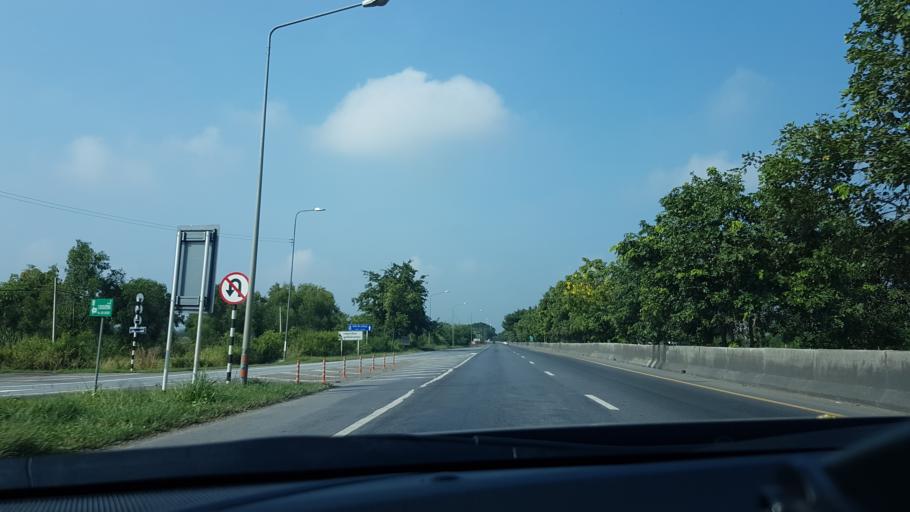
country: TH
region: Phra Nakhon Si Ayutthaya
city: Bang Pa-in
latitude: 14.1466
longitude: 100.5502
